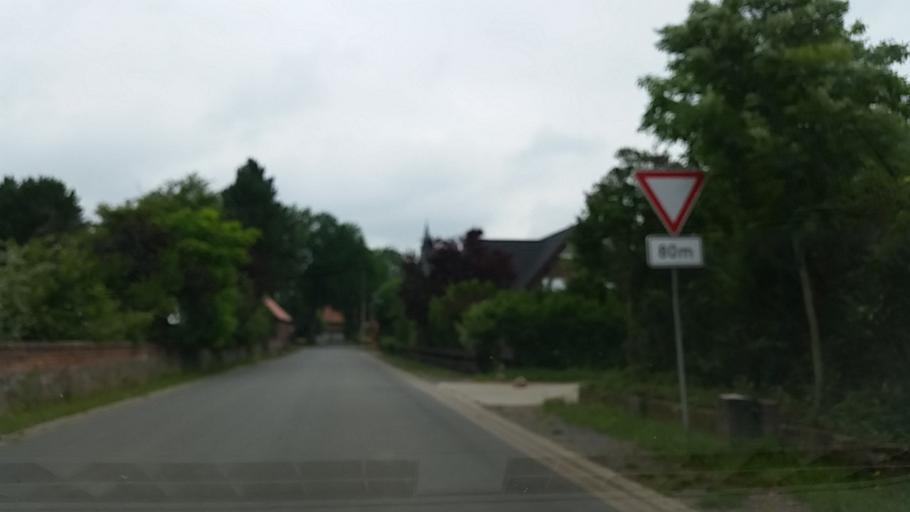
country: DE
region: Lower Saxony
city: Wieren
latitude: 52.9083
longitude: 10.6663
